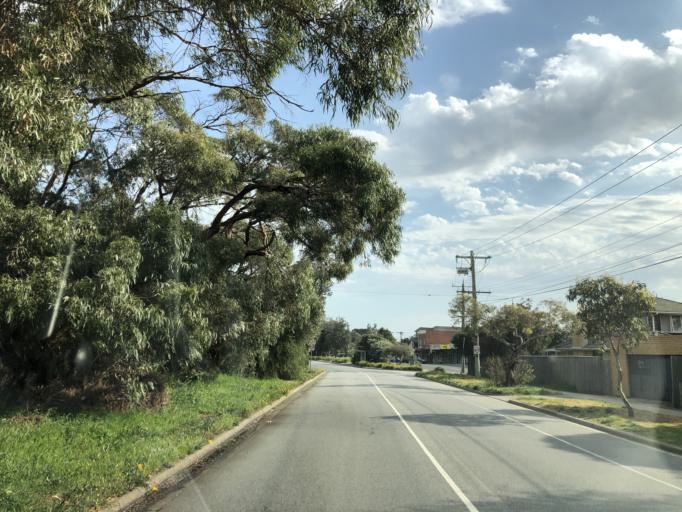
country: AU
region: Victoria
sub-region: Kingston
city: Carrum
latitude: -38.0904
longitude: 145.1282
